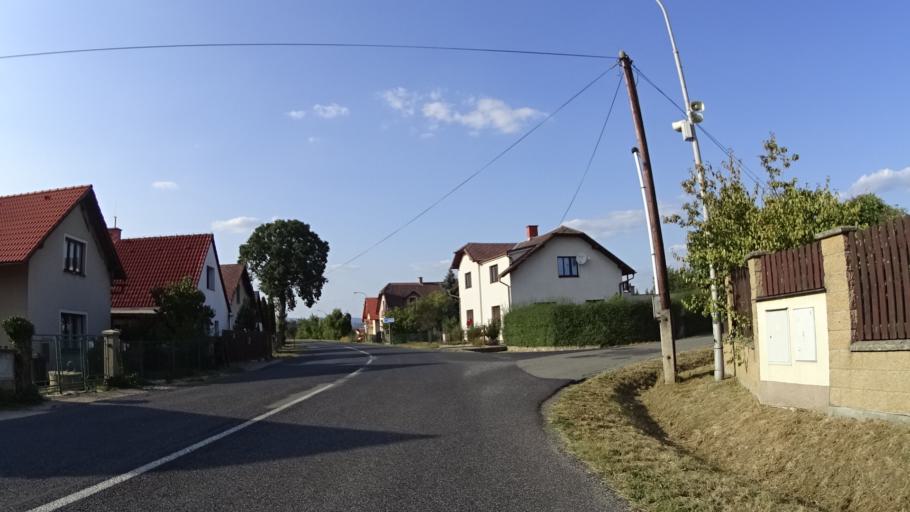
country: CZ
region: Central Bohemia
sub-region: Okres Mlada Boleslav
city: Zd'ar
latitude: 50.5580
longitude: 15.0685
